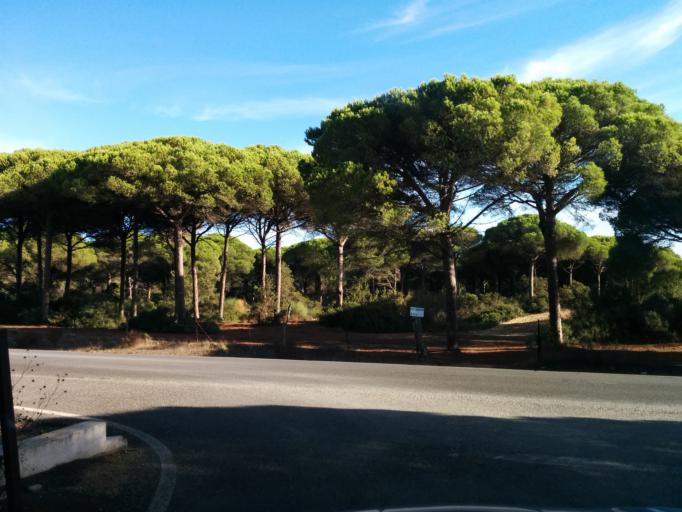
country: ES
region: Andalusia
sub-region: Provincia de Cadiz
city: Vejer de la Frontera
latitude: 36.1936
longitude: -5.9935
